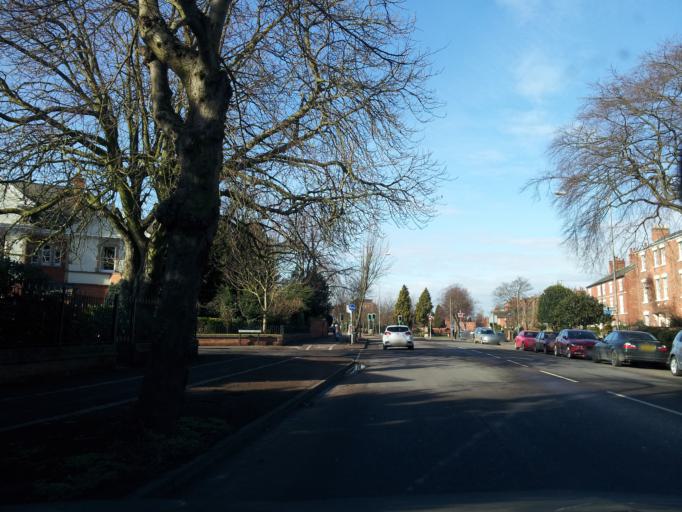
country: GB
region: England
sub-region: Nottinghamshire
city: Newark on Trent
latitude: 53.0709
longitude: -0.8014
